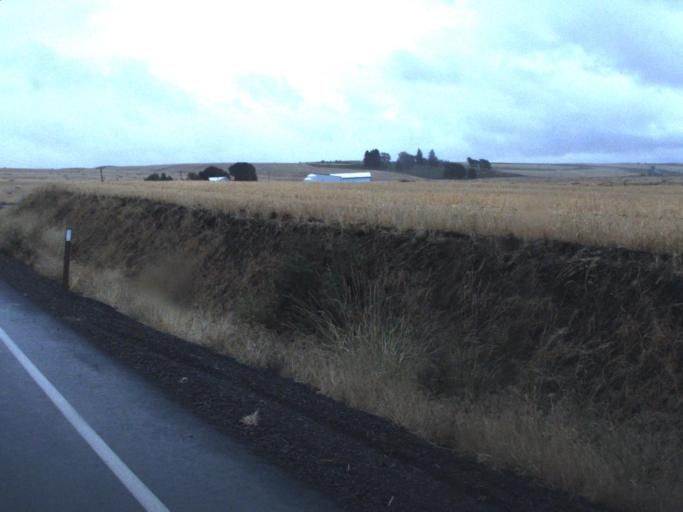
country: US
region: Washington
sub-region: Whitman County
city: Colfax
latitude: 47.0860
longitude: -117.5499
